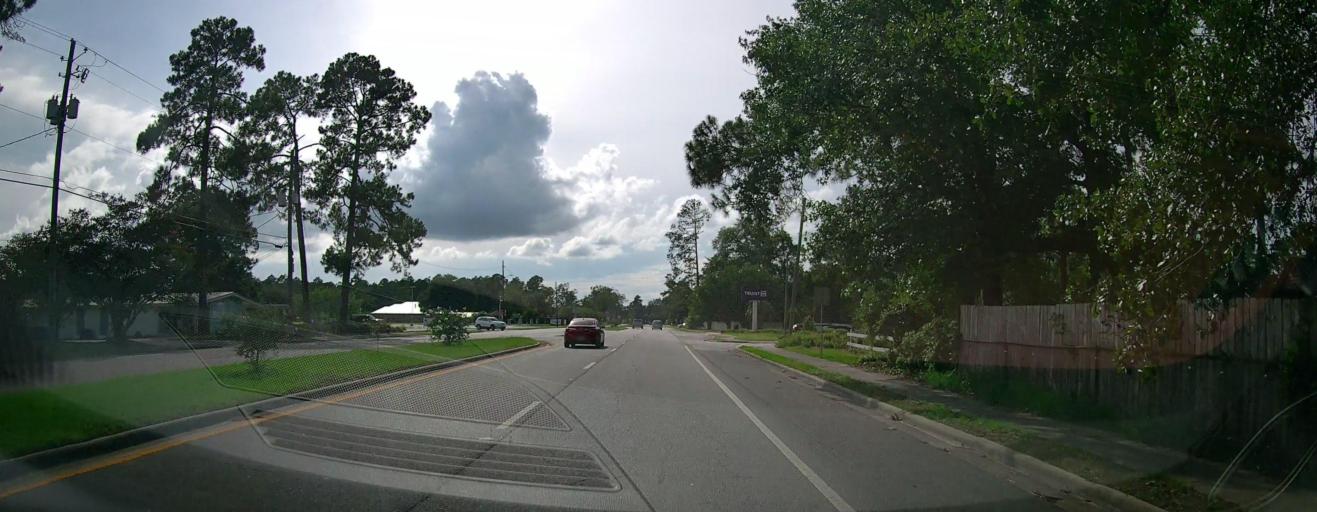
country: US
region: Georgia
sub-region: Wayne County
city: Jesup
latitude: 31.6021
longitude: -81.8963
